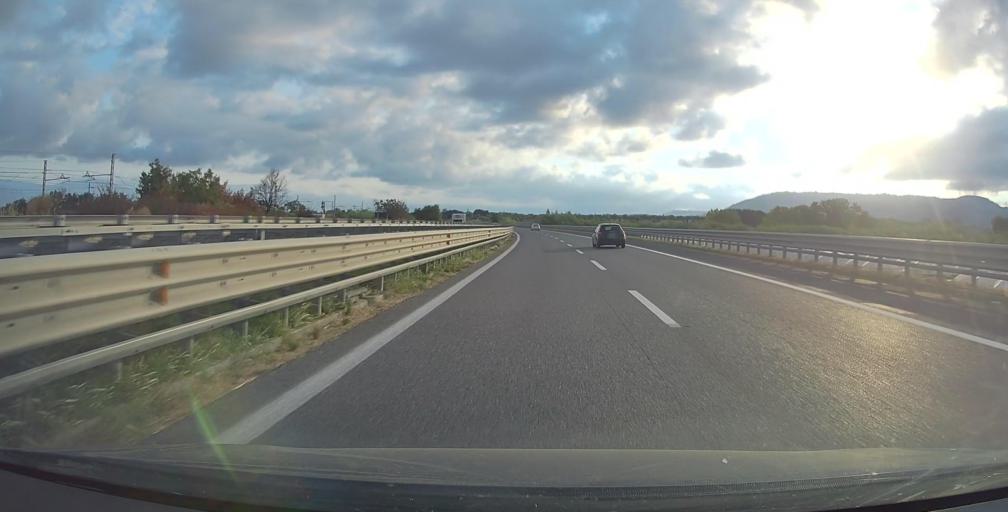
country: IT
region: Calabria
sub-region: Provincia di Catanzaro
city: Acconia
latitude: 38.8243
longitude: 16.2495
